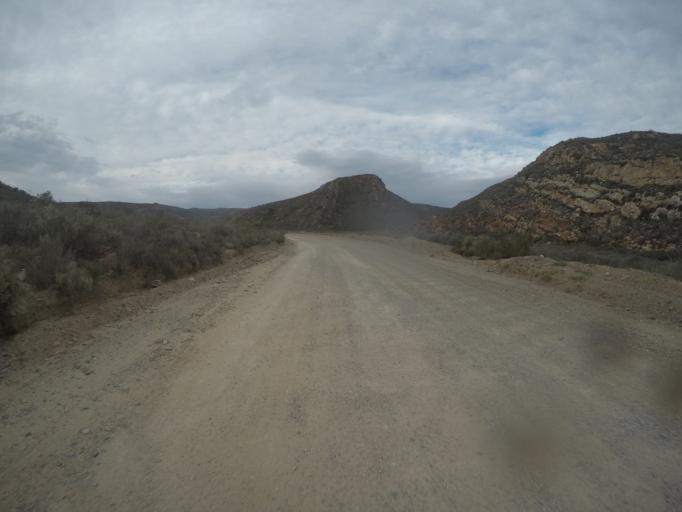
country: ZA
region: Eastern Cape
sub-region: Cacadu District Municipality
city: Willowmore
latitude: -33.5022
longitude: 23.6362
